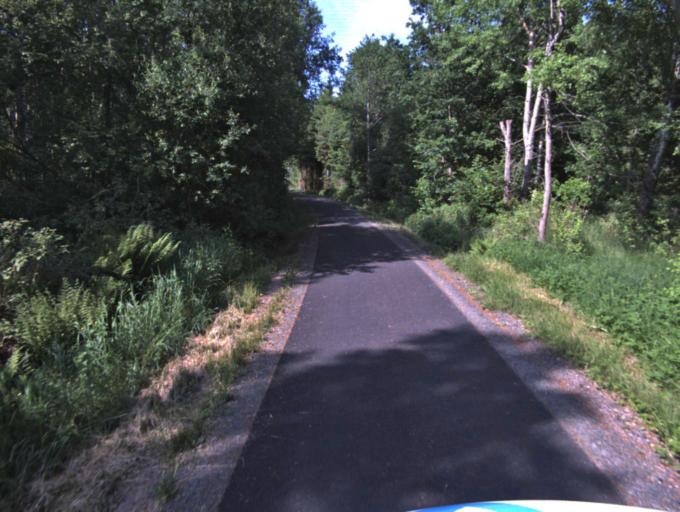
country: SE
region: Skane
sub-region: Kristianstads Kommun
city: Tollarp
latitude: 56.1965
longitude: 14.2893
